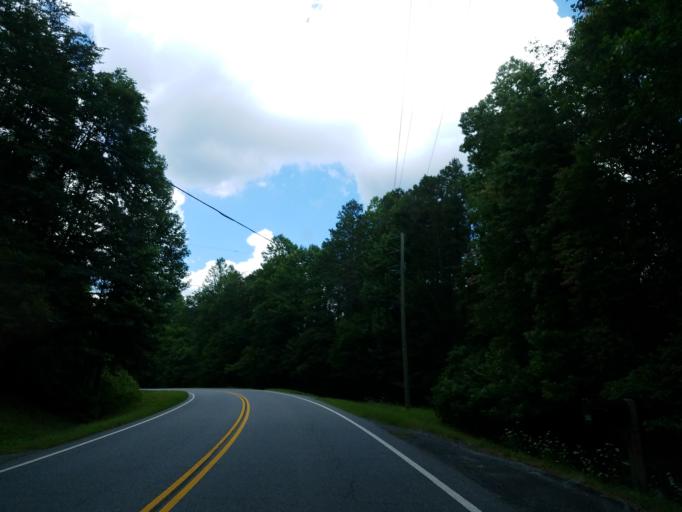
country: US
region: Georgia
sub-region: Lumpkin County
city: Dahlonega
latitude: 34.5121
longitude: -84.0637
